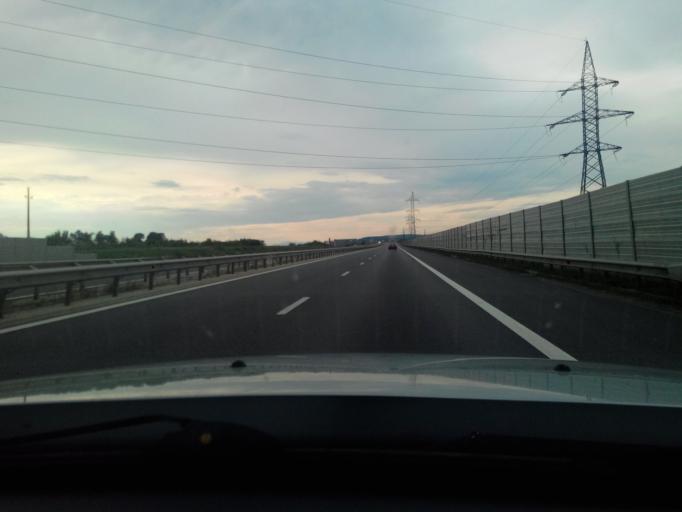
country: RO
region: Arges
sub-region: Comuna Albestii de Arges
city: Pitesti
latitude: 44.8559
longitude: 24.8937
